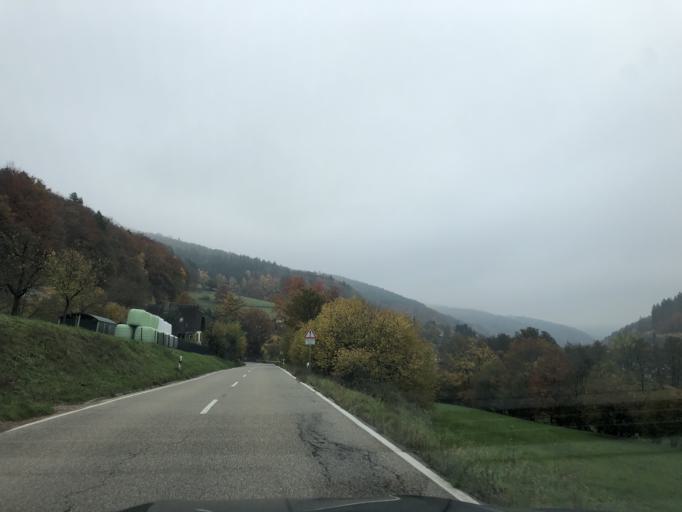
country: DE
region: Baden-Wuerttemberg
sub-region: Karlsruhe Region
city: Heiligkreuzsteinach
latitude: 49.4713
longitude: 8.8004
